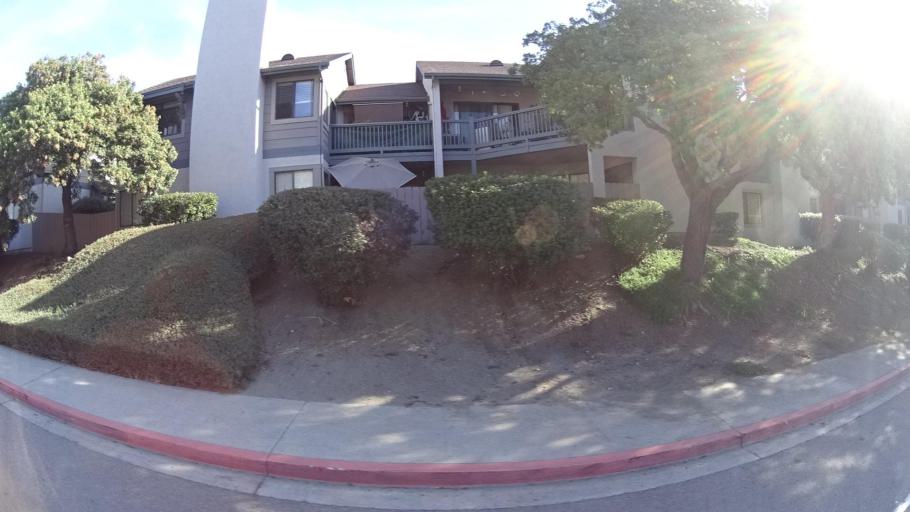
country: US
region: California
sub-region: San Diego County
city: Rancho San Diego
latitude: 32.7322
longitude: -116.9619
